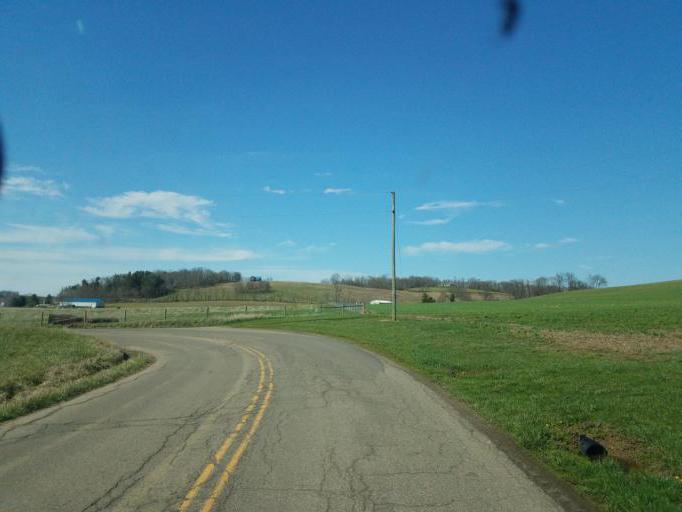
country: US
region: Ohio
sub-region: Knox County
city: Danville
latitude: 40.4363
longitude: -82.2535
